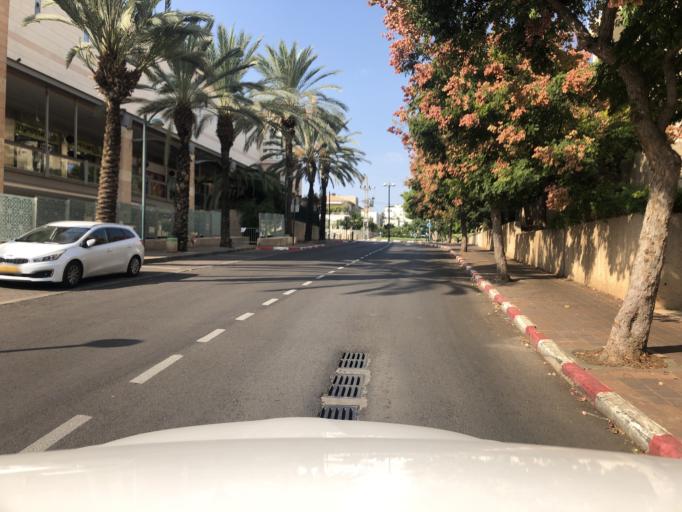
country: IL
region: Central District
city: Kfar Saba
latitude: 32.1789
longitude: 34.9043
